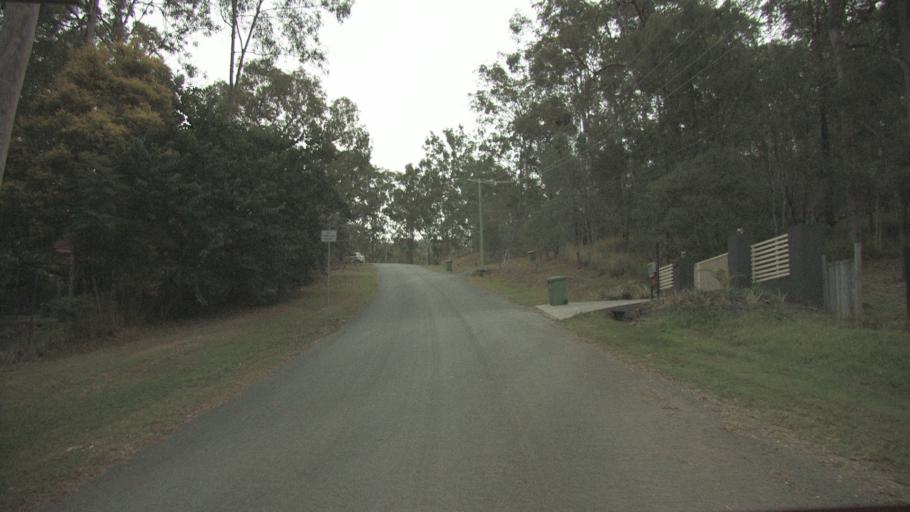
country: AU
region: Queensland
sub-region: Logan
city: Chambers Flat
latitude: -27.8208
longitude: 153.0915
